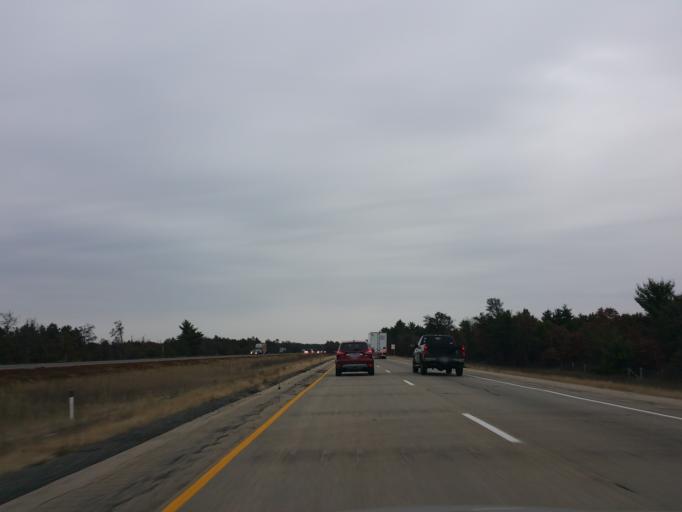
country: US
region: Wisconsin
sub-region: Jackson County
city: Black River Falls
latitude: 44.1892
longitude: -90.6314
